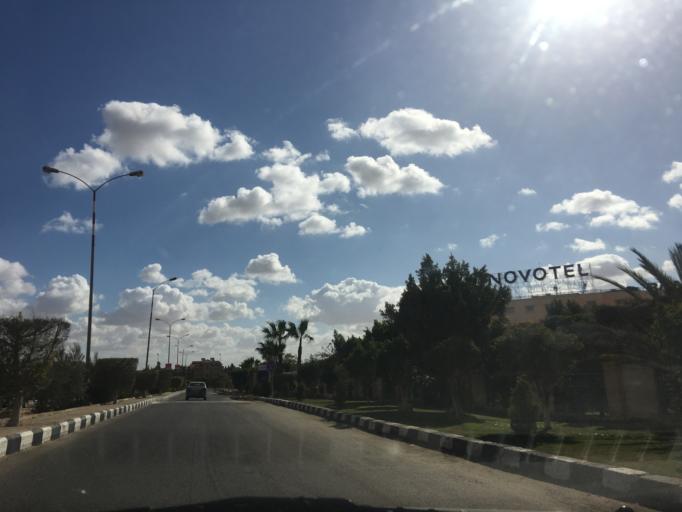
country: EG
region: Al Jizah
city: Madinat Sittah Uktubar
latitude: 29.9977
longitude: 30.9689
